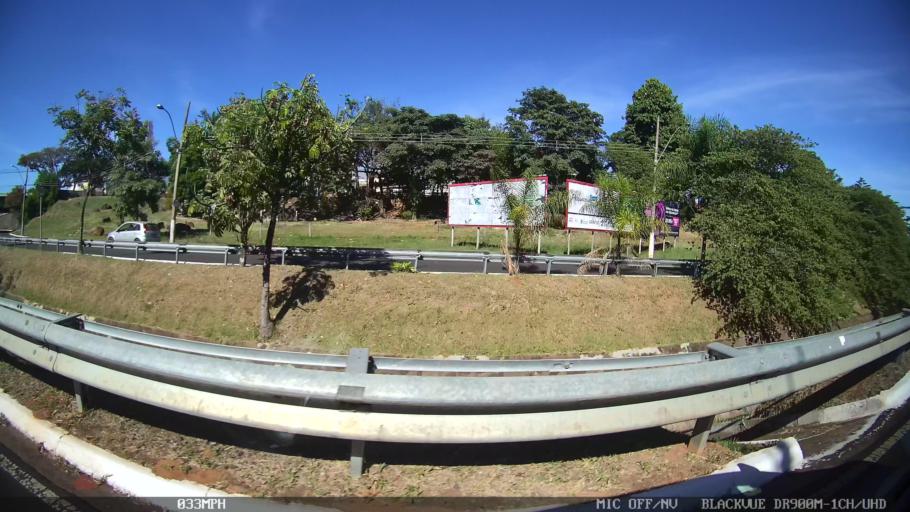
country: BR
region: Sao Paulo
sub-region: Franca
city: Franca
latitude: -20.5197
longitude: -47.3857
